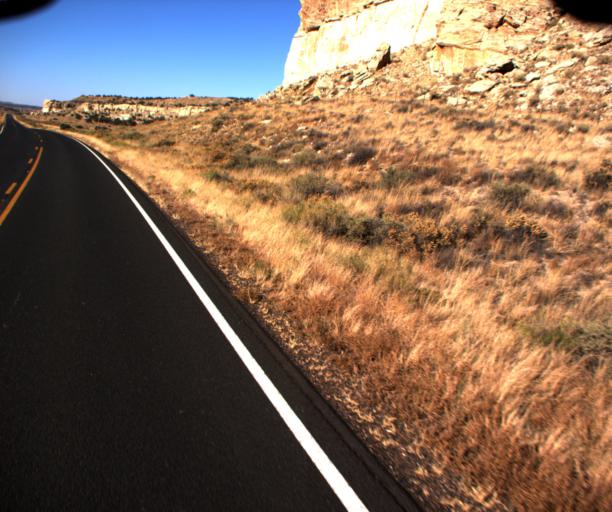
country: US
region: Arizona
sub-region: Apache County
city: Ganado
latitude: 35.7552
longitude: -109.8362
